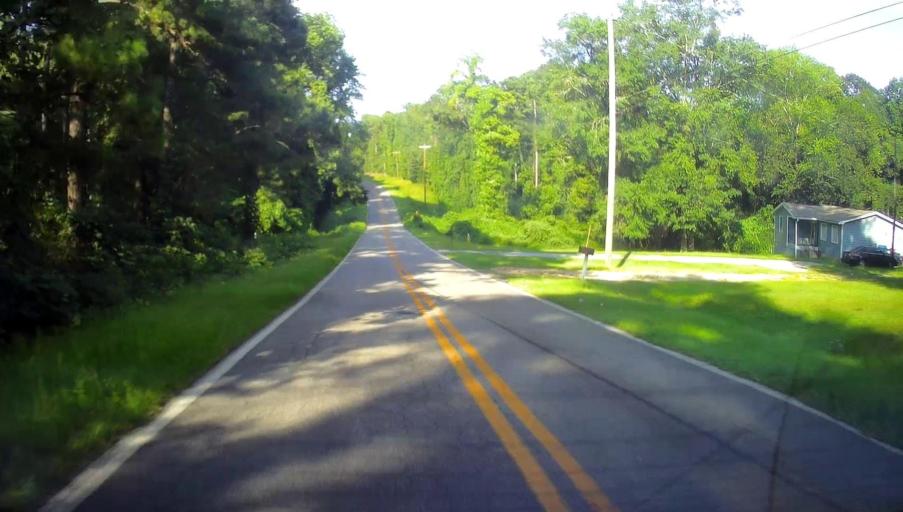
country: US
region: Georgia
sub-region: Bibb County
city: West Point
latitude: 32.7897
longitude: -83.8142
